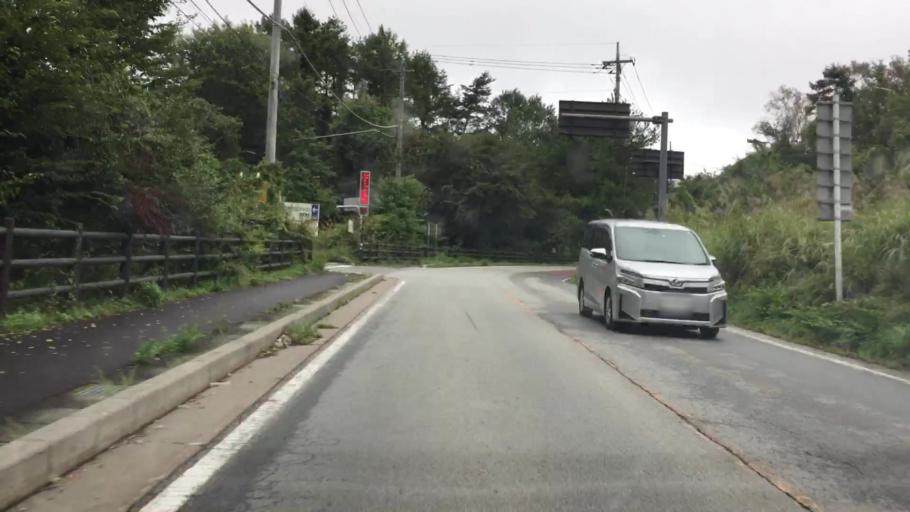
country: JP
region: Yamanashi
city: Fujikawaguchiko
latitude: 35.4768
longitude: 138.6803
